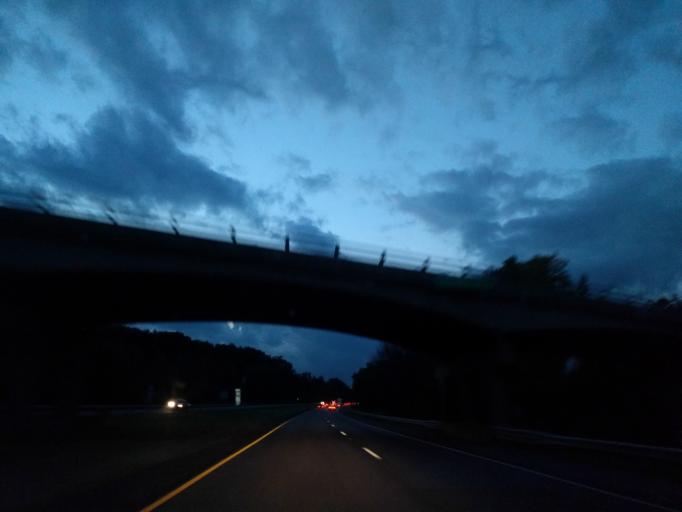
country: US
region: Indiana
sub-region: Boone County
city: Zionsville
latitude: 39.8900
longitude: -86.3043
